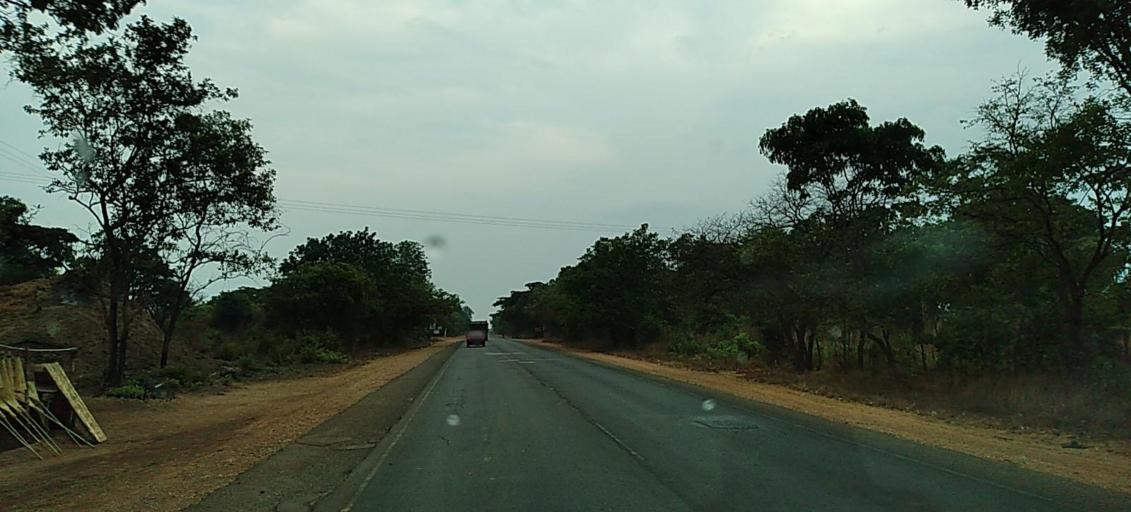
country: ZM
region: Copperbelt
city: Luanshya
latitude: -13.0526
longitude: 28.4621
